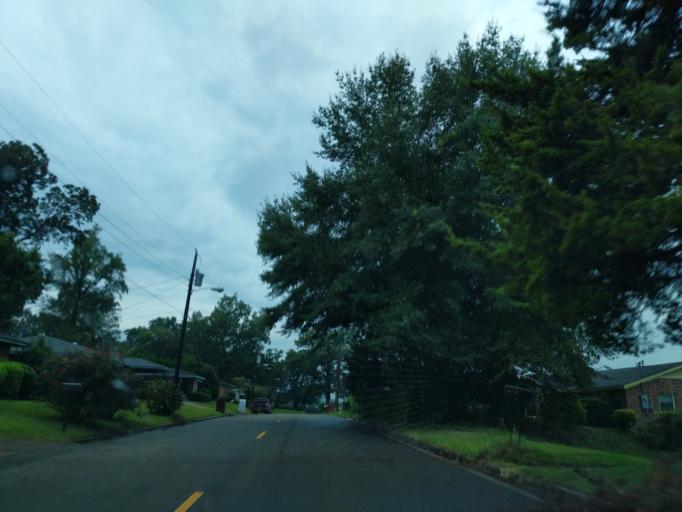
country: US
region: Mississippi
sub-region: Warren County
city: Vicksburg
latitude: 32.3358
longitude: -90.8900
